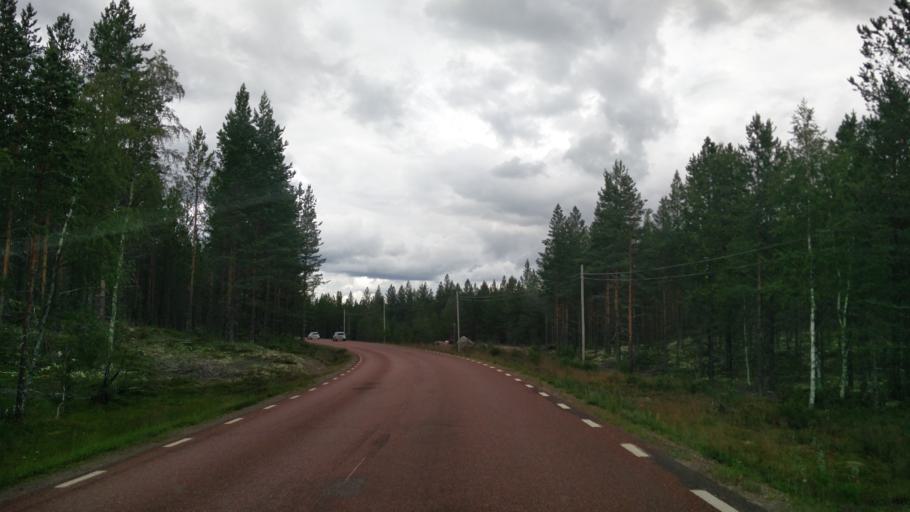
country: NO
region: Hedmark
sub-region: Trysil
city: Innbygda
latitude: 61.1426
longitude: 12.8076
